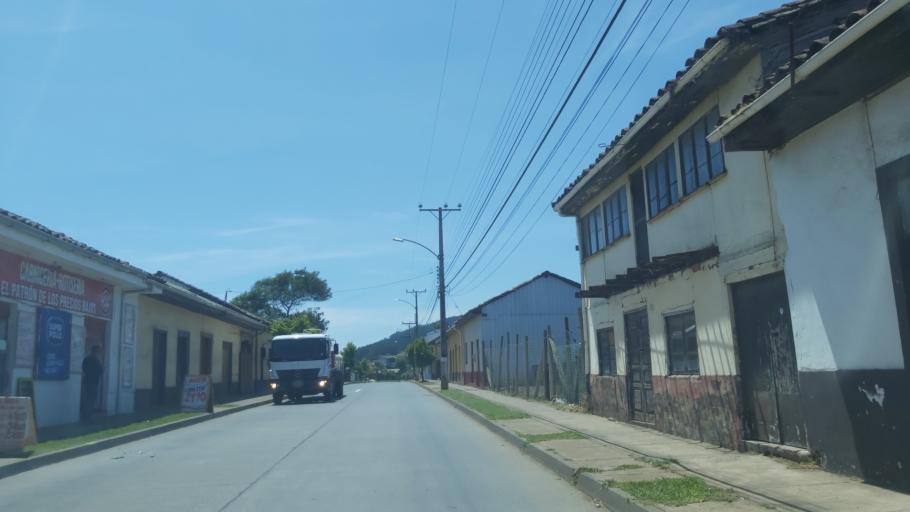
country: CL
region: Maule
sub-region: Provincia de Cauquenes
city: Cauquenes
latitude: -35.8452
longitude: -72.6355
